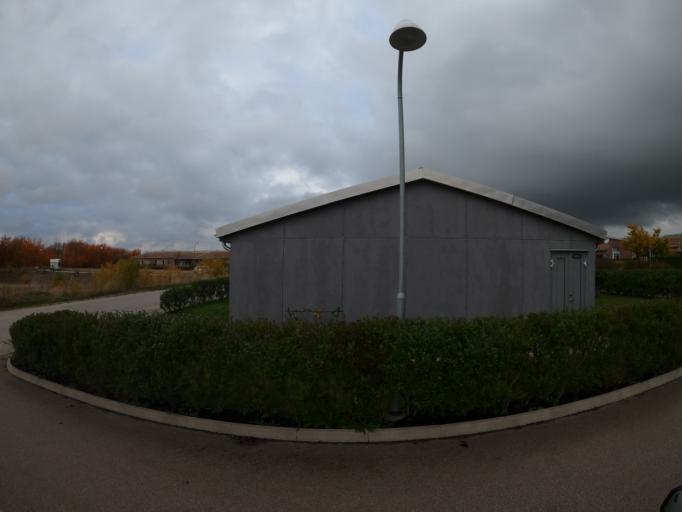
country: SE
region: Skane
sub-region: Lunds Kommun
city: Genarp
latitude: 55.6595
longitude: 13.3549
